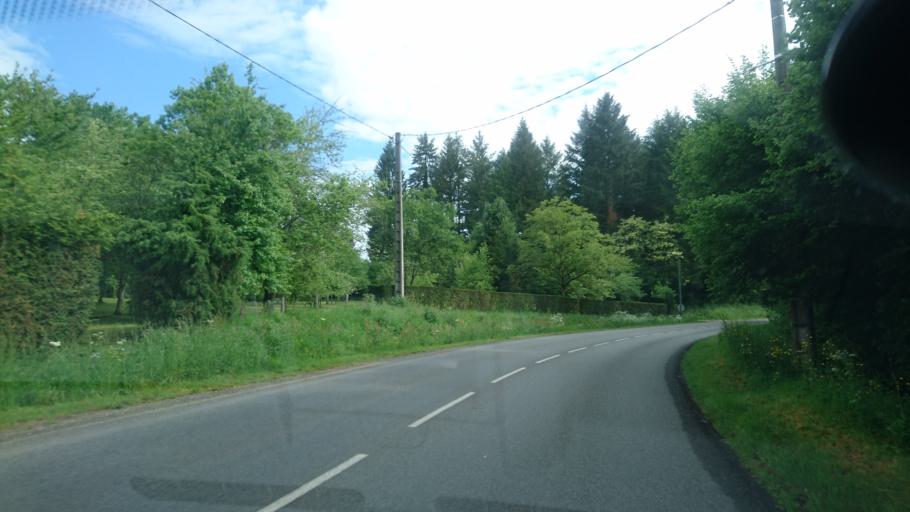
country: FR
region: Limousin
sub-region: Departement de la Haute-Vienne
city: Peyrat-le-Chateau
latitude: 45.8022
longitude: 1.7645
